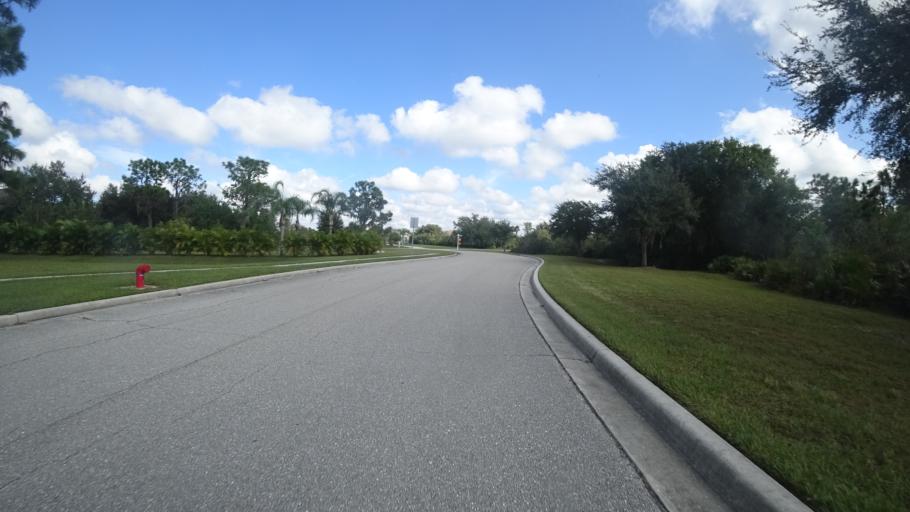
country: US
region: Florida
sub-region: Sarasota County
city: Fruitville
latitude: 27.3918
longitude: -82.3043
